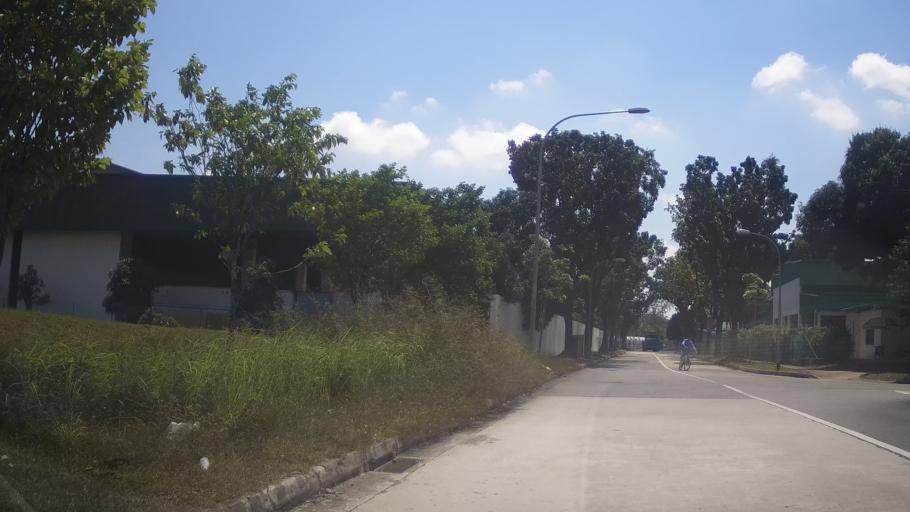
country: SG
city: Singapore
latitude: 1.3148
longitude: 103.7248
